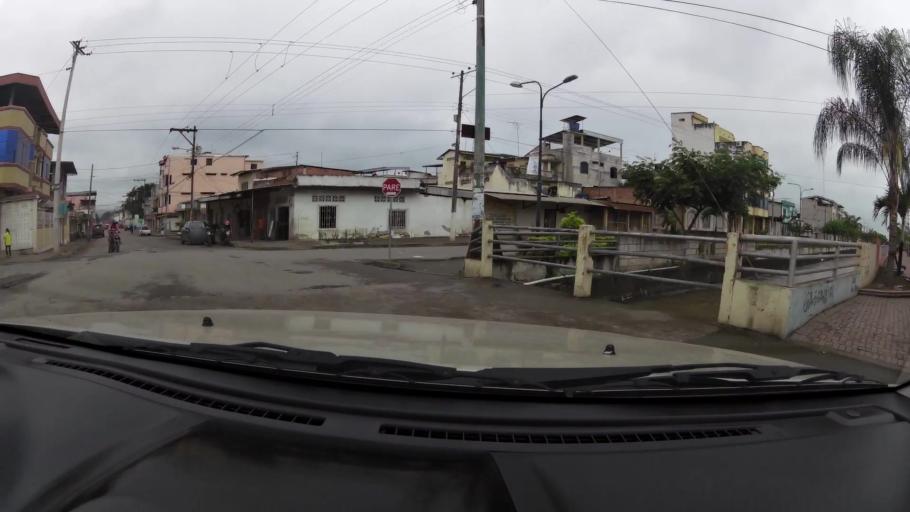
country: EC
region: El Oro
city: Pasaje
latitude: -3.3317
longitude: -79.8091
